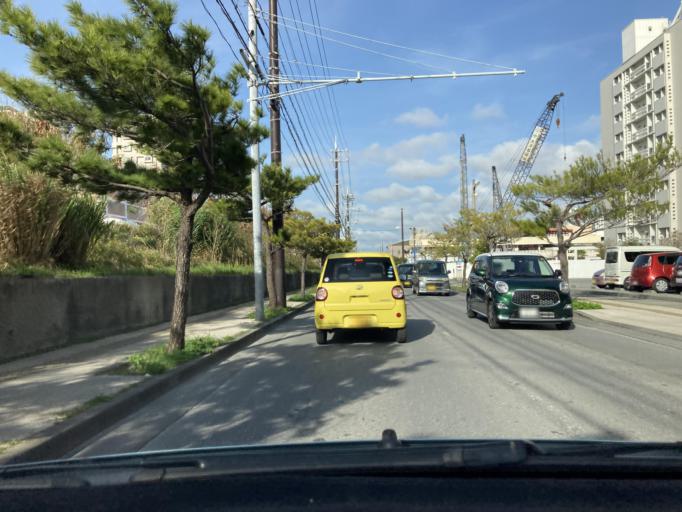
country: JP
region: Okinawa
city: Naha-shi
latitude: 26.2276
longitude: 127.6896
